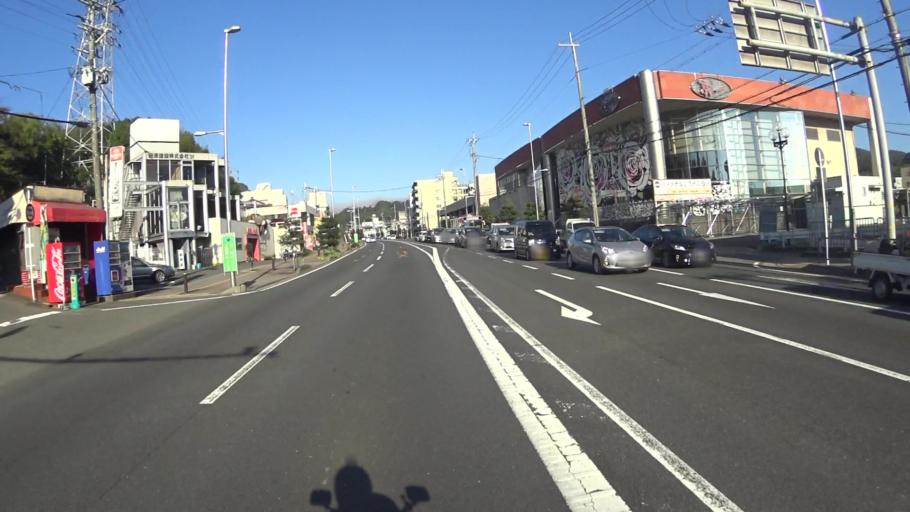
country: JP
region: Kyoto
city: Muko
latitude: 34.9737
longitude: 135.6689
